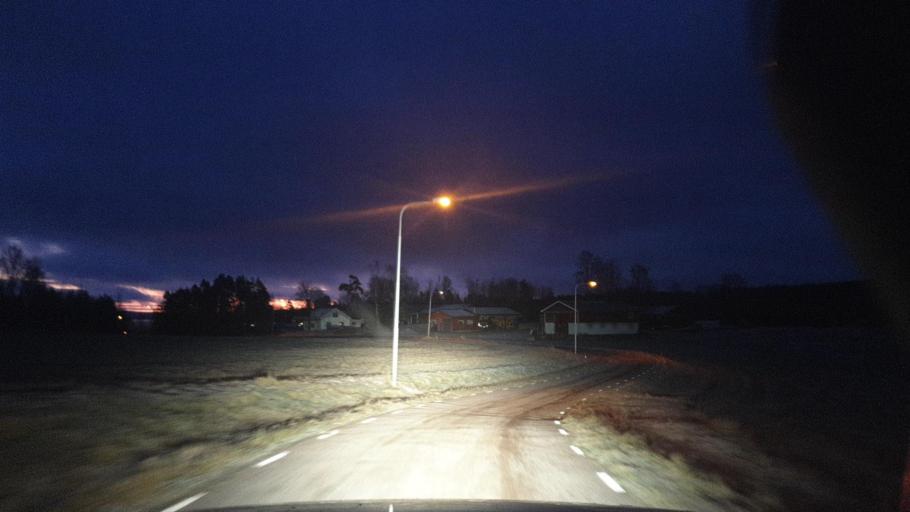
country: SE
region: Vaermland
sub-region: Arvika Kommun
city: Arvika
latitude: 59.5512
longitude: 12.5747
